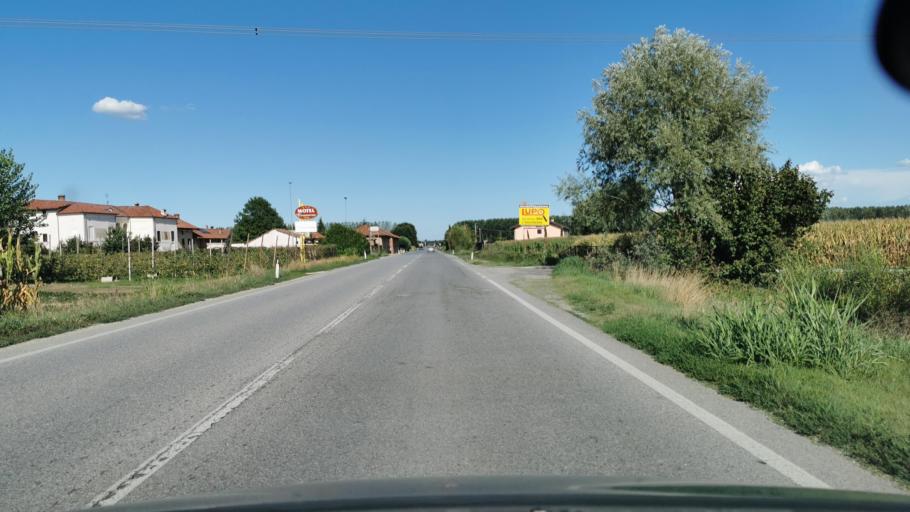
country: IT
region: Piedmont
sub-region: Provincia di Cuneo
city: Marene
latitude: 44.6527
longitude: 7.6960
